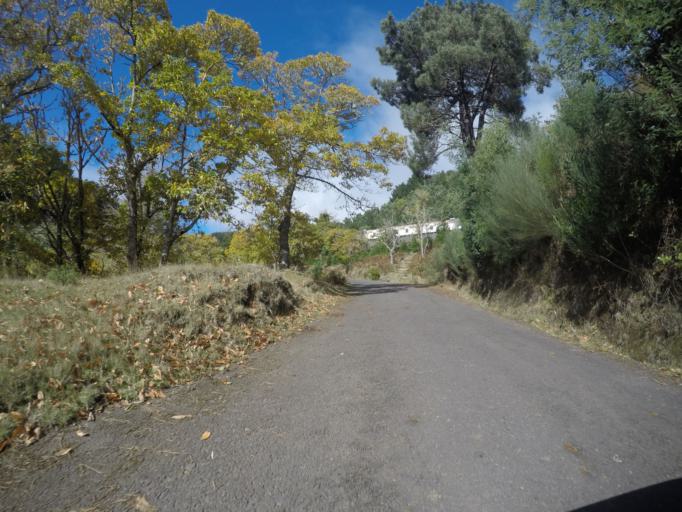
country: PT
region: Madeira
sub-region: Funchal
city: Nossa Senhora do Monte
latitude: 32.7016
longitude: -16.8862
